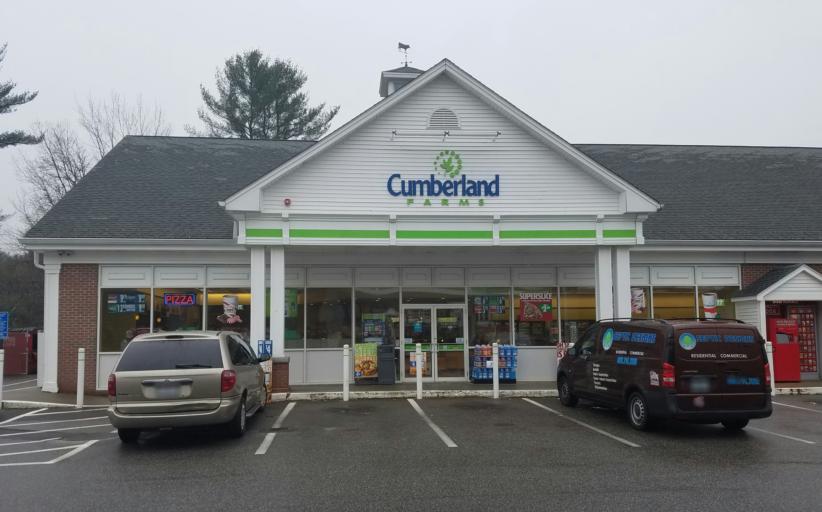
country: US
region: New Hampshire
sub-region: Merrimack County
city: Epsom
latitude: 43.2249
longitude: -71.3454
